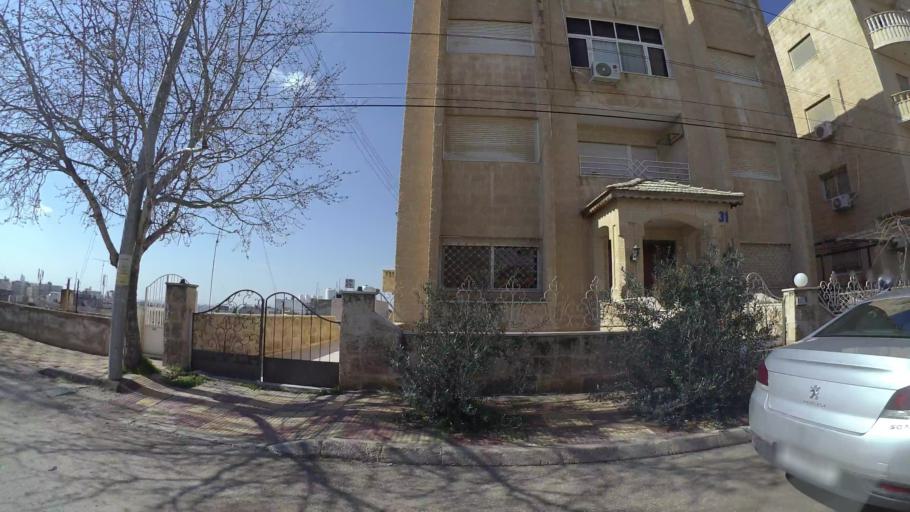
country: JO
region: Amman
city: Al Jubayhah
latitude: 31.9986
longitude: 35.8942
